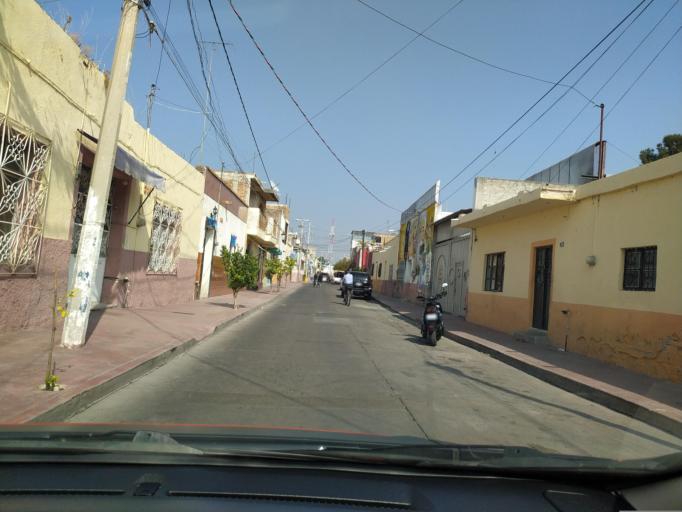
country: MX
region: Guanajuato
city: San Francisco del Rincon
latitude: 21.0281
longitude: -101.8796
